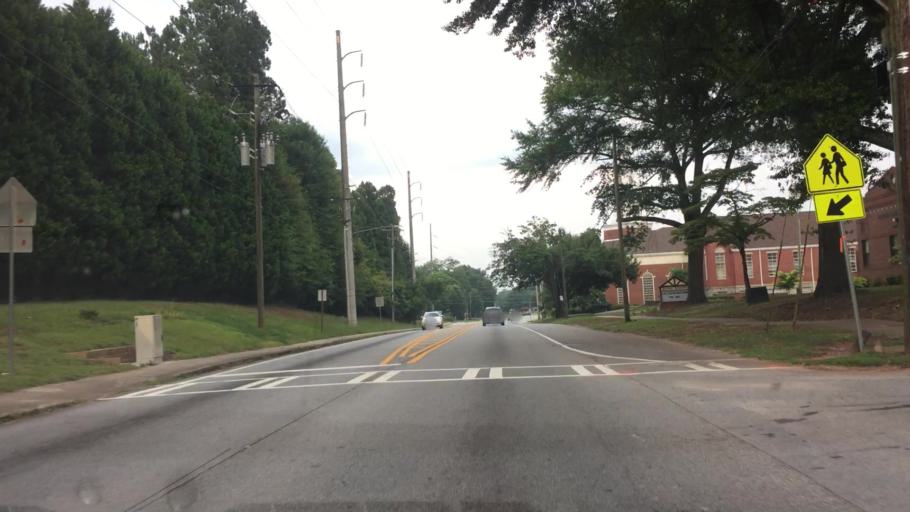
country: US
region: Georgia
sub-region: DeKalb County
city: Avondale Estates
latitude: 33.7748
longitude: -84.2621
